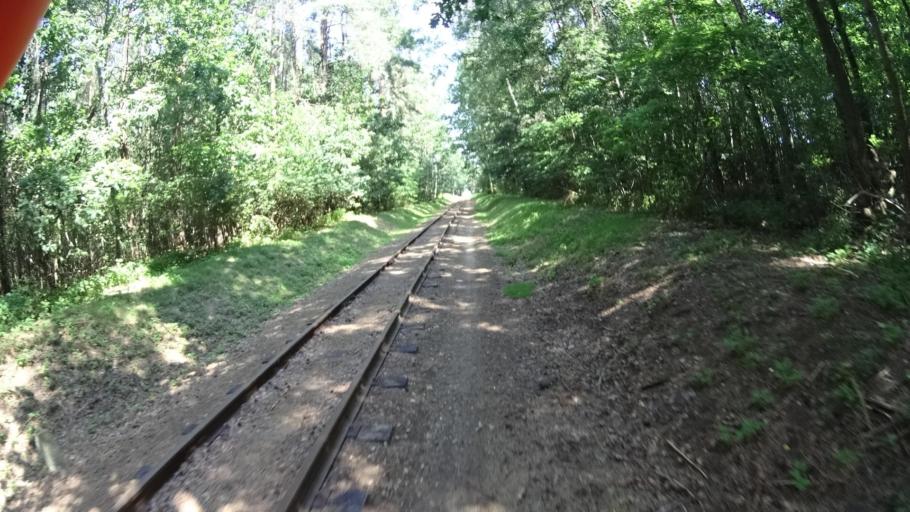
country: PL
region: Masovian Voivodeship
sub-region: Powiat piaseczynski
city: Tarczyn
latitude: 51.9950
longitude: 20.8960
